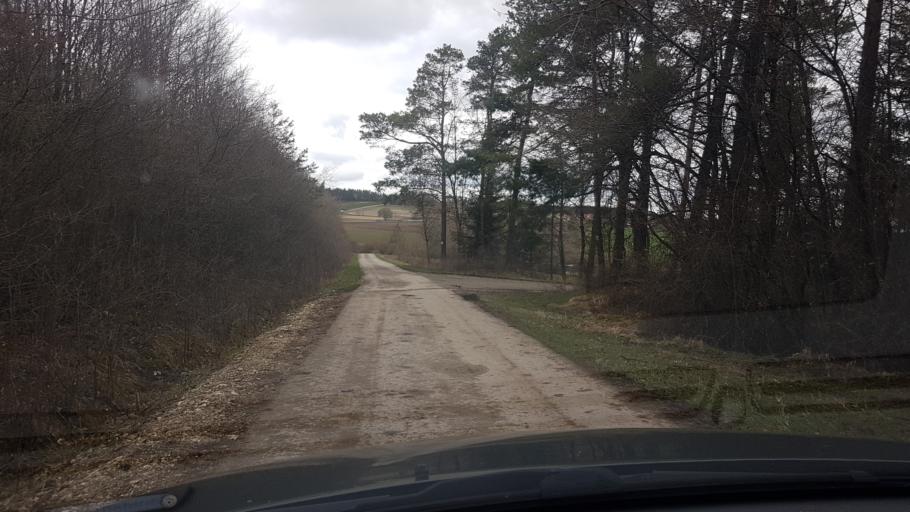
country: DE
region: Bavaria
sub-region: Upper Franconia
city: Poxdorf
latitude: 49.8645
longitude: 11.0944
